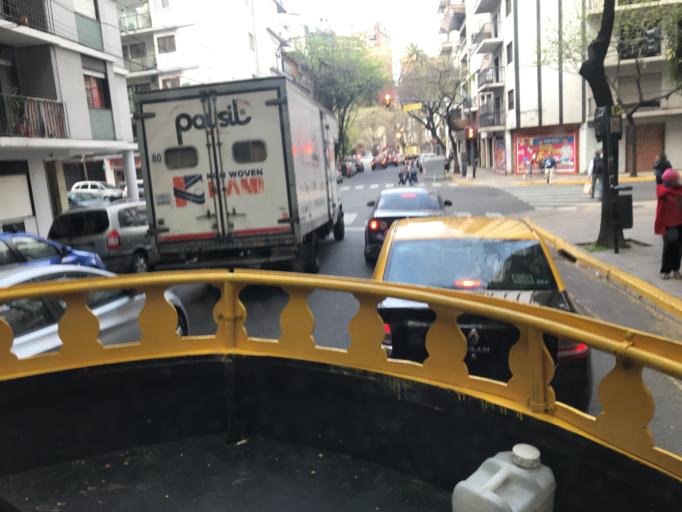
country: AR
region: Buenos Aires F.D.
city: Retiro
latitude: -34.5907
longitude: -58.4173
